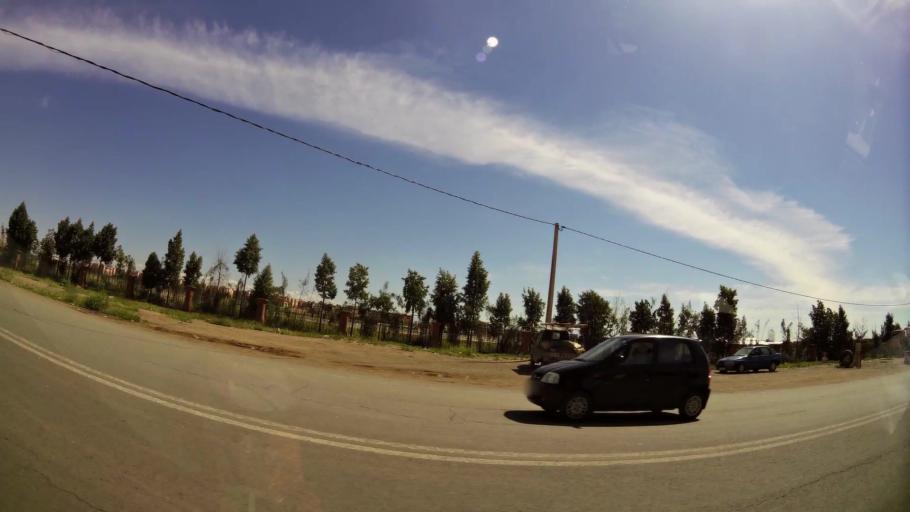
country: MA
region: Marrakech-Tensift-Al Haouz
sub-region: Marrakech
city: Marrakesh
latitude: 31.6404
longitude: -8.0999
